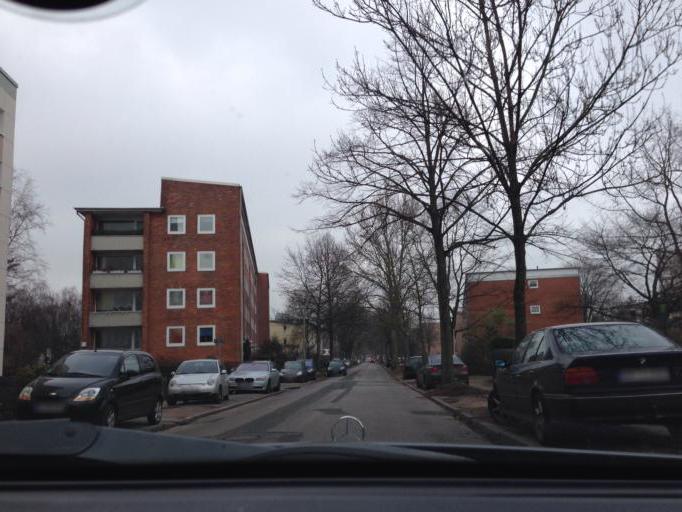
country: DE
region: Hamburg
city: Marienthal
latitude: 53.5917
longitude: 10.0875
